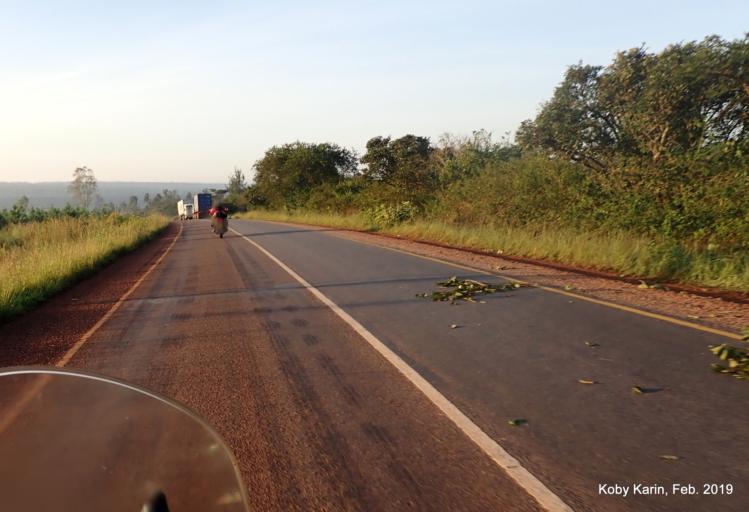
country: TZ
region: Kagera
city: Ngara
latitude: -2.5272
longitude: 30.8551
